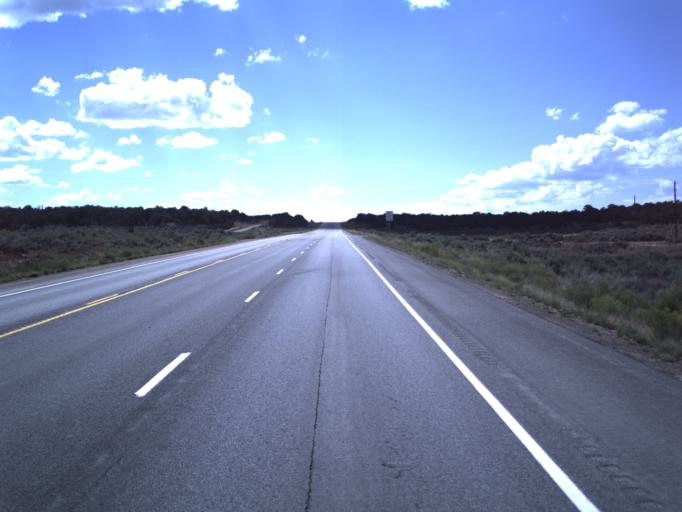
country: US
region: Utah
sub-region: Duchesne County
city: Duchesne
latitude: 40.1806
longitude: -110.6224
